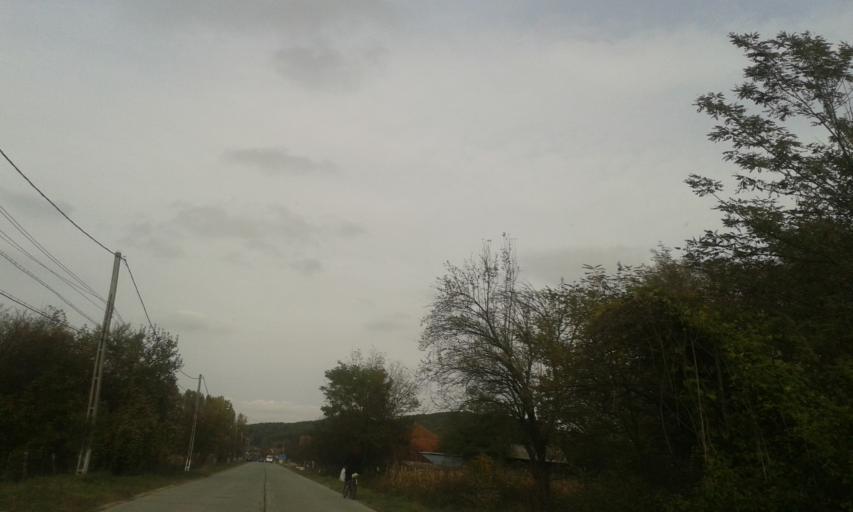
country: RO
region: Gorj
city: Logresti
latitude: 44.8841
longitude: 23.7129
